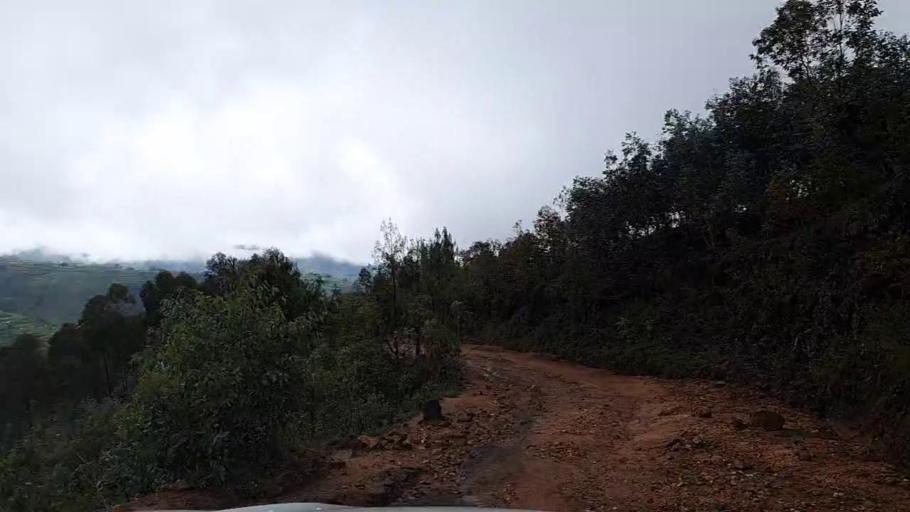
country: RW
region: Southern Province
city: Nzega
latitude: -2.3949
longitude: 29.4988
